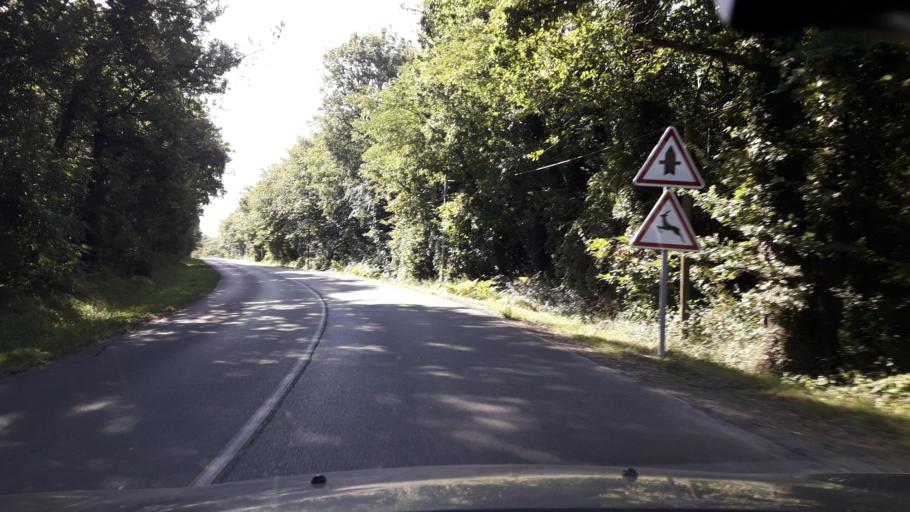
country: FR
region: Poitou-Charentes
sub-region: Departement de la Charente-Maritime
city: Etaules
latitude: 45.7249
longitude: -1.0898
